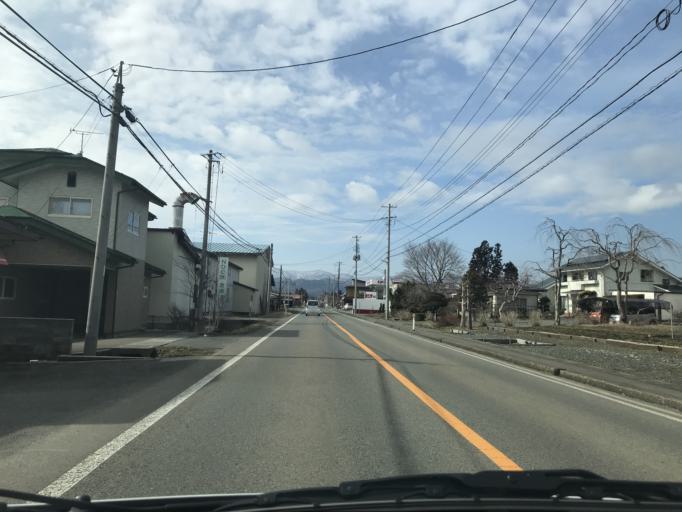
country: JP
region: Iwate
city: Hanamaki
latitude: 39.3817
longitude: 141.0768
